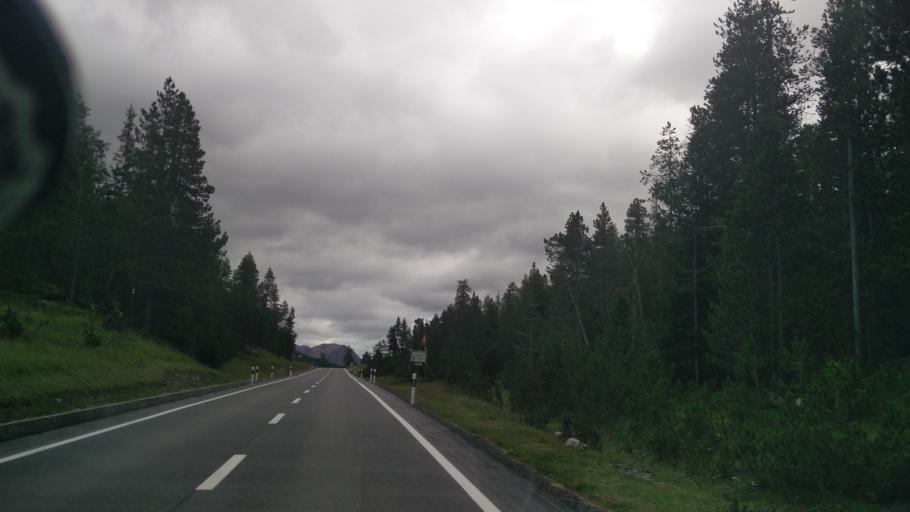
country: CH
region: Grisons
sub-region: Inn District
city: Zernez
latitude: 46.6807
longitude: 10.1586
